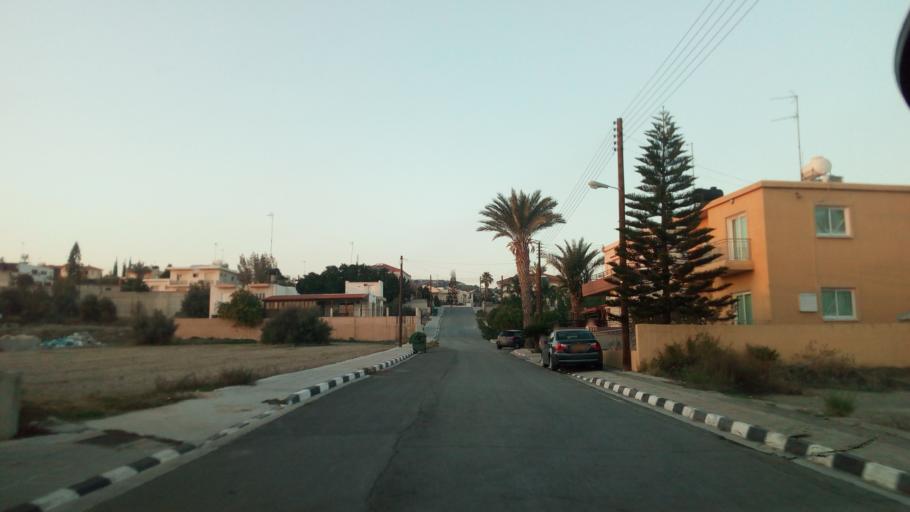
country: CY
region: Larnaka
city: Kofinou
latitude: 34.8548
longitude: 33.4599
